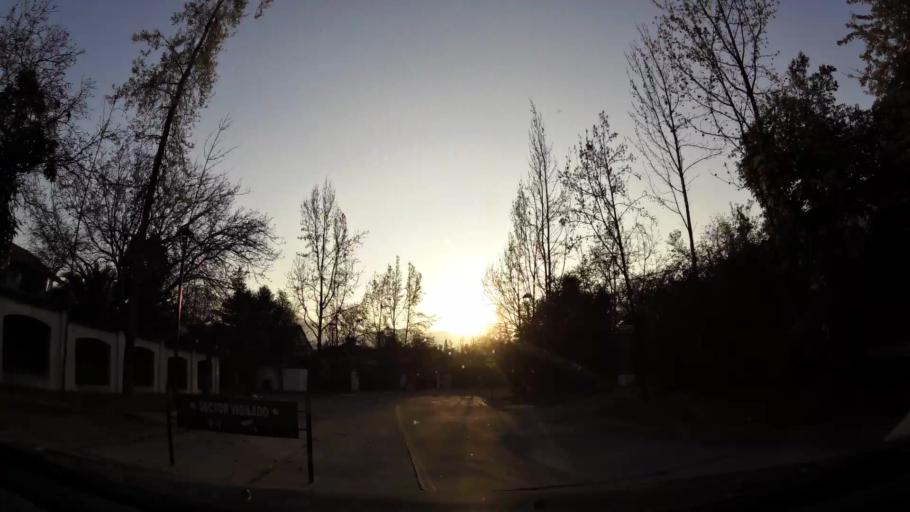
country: CL
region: Santiago Metropolitan
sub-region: Provincia de Santiago
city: Villa Presidente Frei, Nunoa, Santiago, Chile
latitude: -33.3359
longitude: -70.5281
